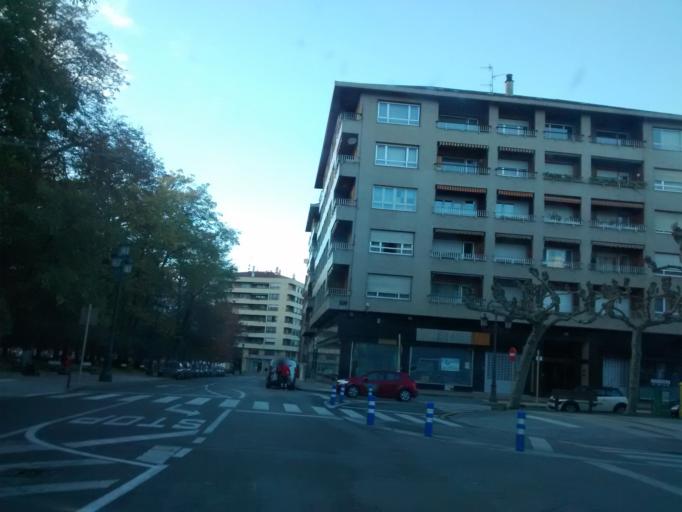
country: ES
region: Cantabria
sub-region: Provincia de Cantabria
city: Torrelavega
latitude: 43.3459
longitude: -4.0522
